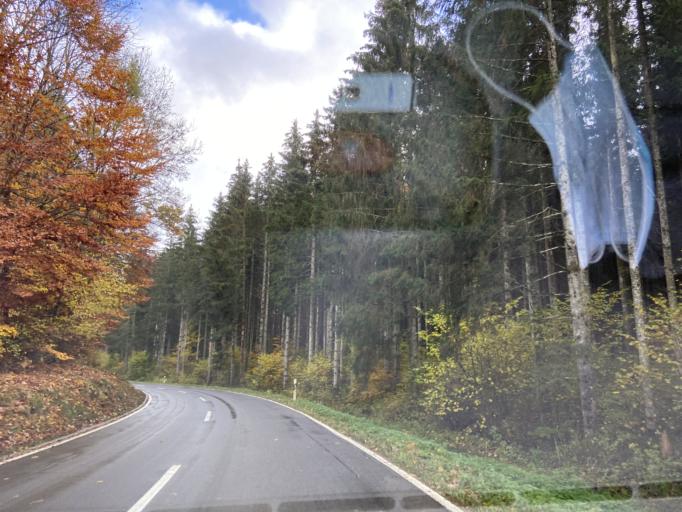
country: DE
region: Baden-Wuerttemberg
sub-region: Tuebingen Region
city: Schwenningen
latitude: 48.0993
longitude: 9.0135
